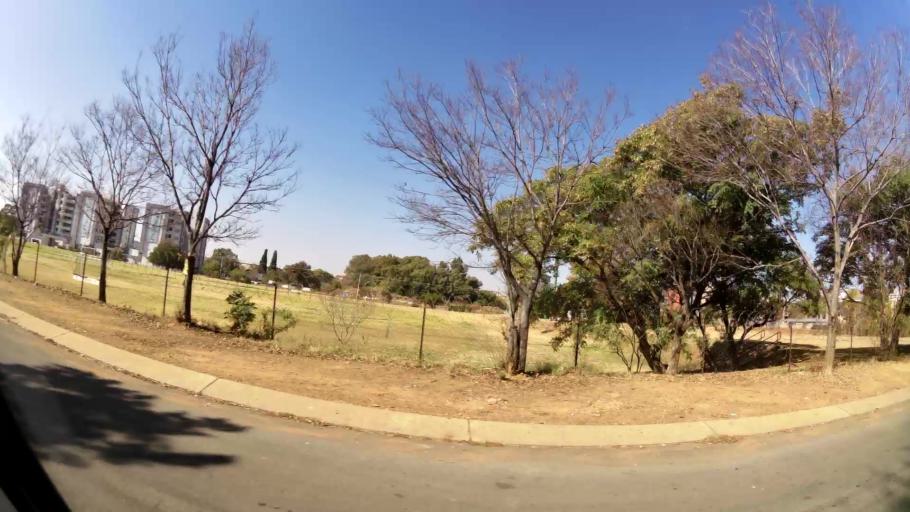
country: ZA
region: Gauteng
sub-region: City of Tshwane Metropolitan Municipality
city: Pretoria
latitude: -25.7825
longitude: 28.2660
